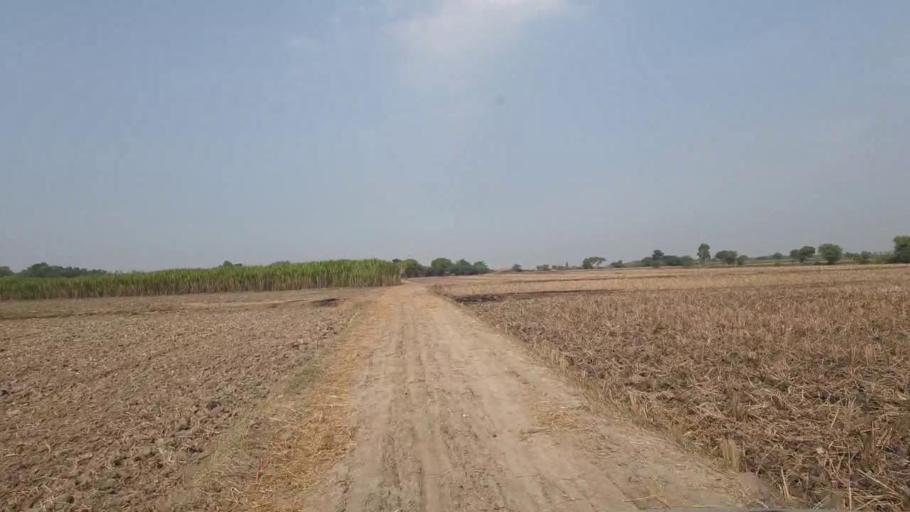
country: PK
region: Sindh
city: Matli
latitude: 24.9880
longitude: 68.7050
